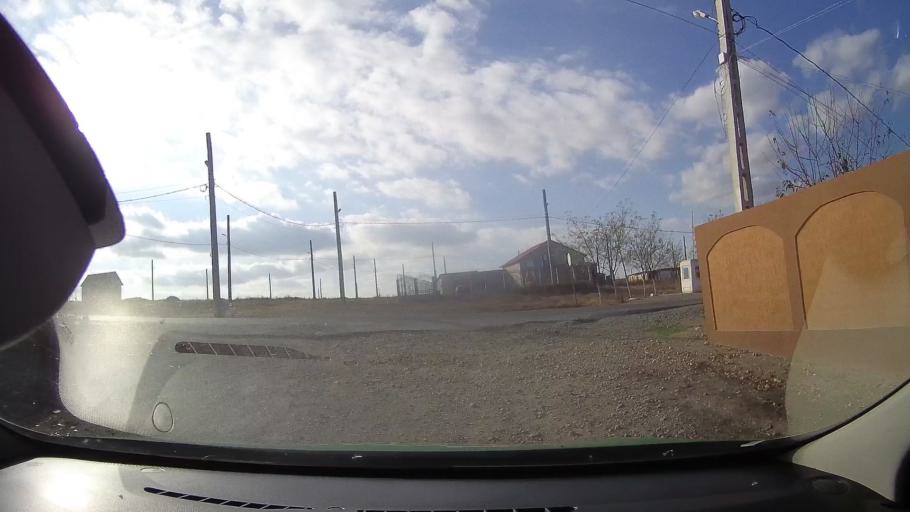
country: RO
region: Constanta
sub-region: Comuna Sacele
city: Sacele
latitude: 44.4806
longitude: 28.6480
